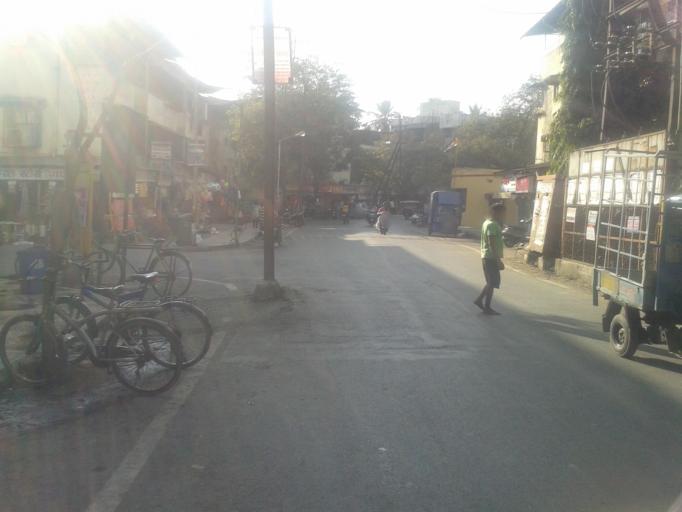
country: IN
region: Maharashtra
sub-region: Thane
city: Dombivli
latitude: 19.2057
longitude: 73.0929
